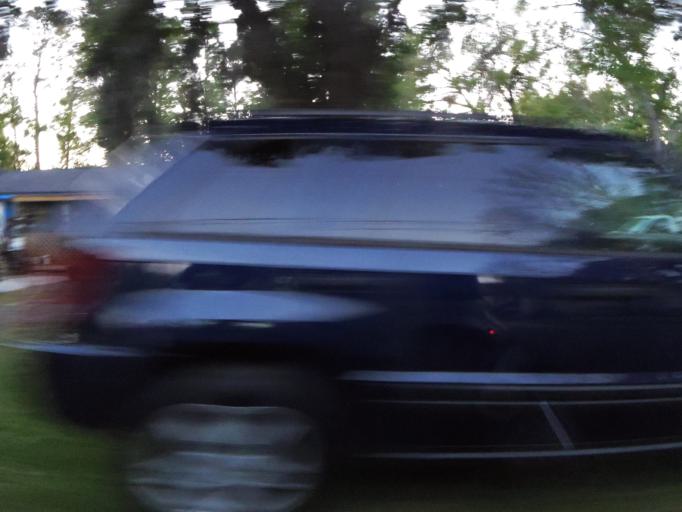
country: US
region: Florida
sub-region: Duval County
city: Jacksonville
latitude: 30.2734
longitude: -81.6307
